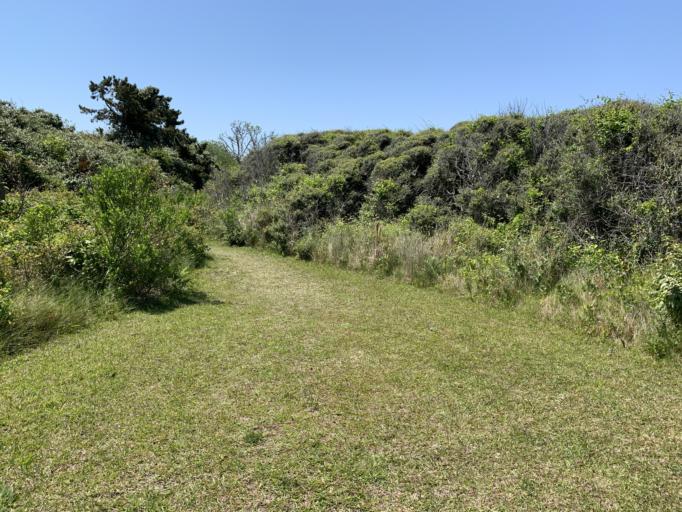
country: US
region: North Carolina
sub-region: Dare County
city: Southern Shores
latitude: 36.2301
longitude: -75.7748
